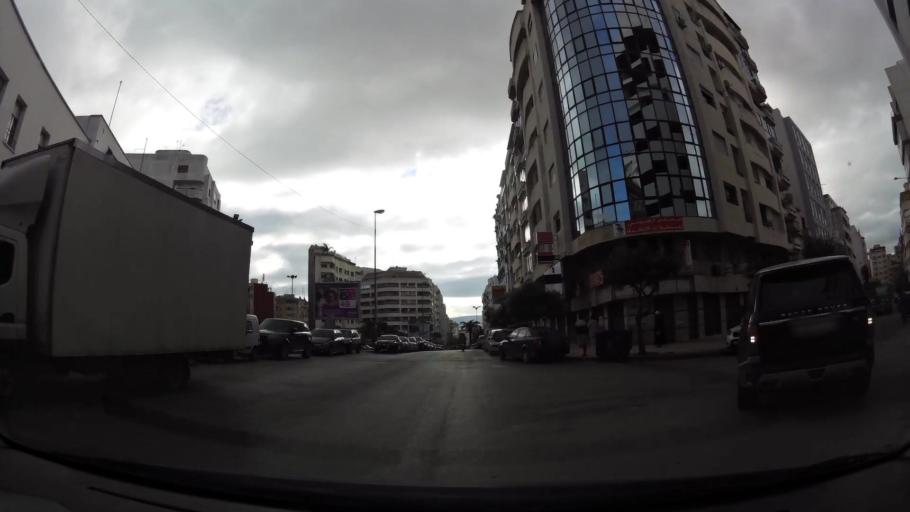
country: MA
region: Tanger-Tetouan
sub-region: Tanger-Assilah
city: Tangier
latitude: 35.7753
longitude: -5.8121
